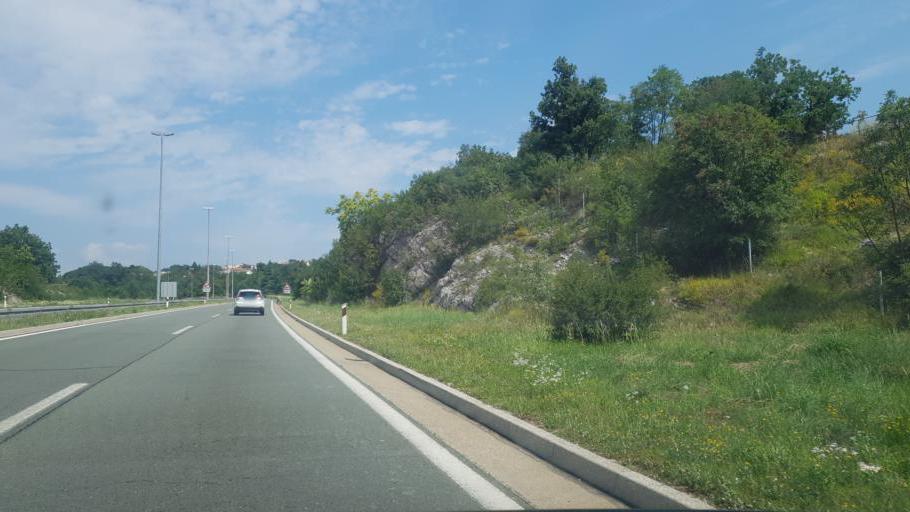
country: HR
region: Primorsko-Goranska
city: Matulji
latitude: 45.3688
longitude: 14.3271
